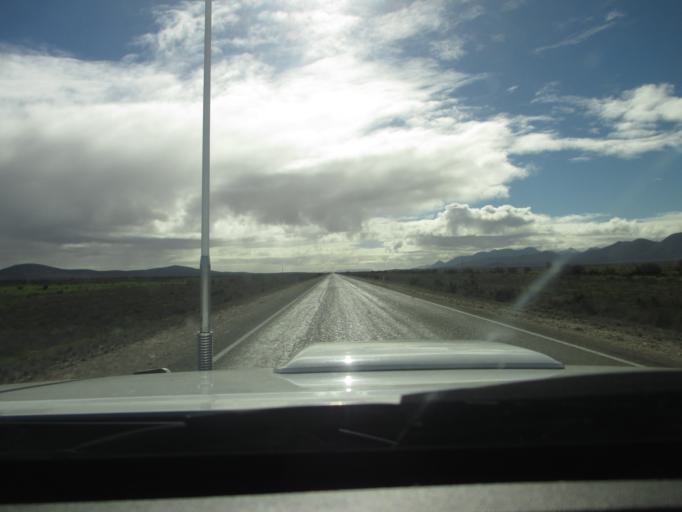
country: AU
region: South Australia
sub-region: Flinders Ranges
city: Quorn
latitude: -31.6838
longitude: 138.3646
